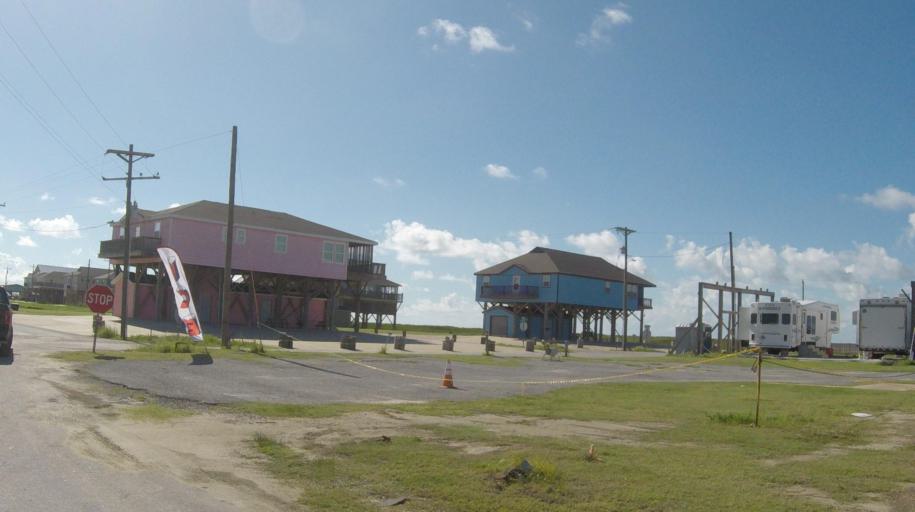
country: US
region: Louisiana
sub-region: Cameron Parish
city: Cameron
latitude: 29.7711
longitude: -93.4597
